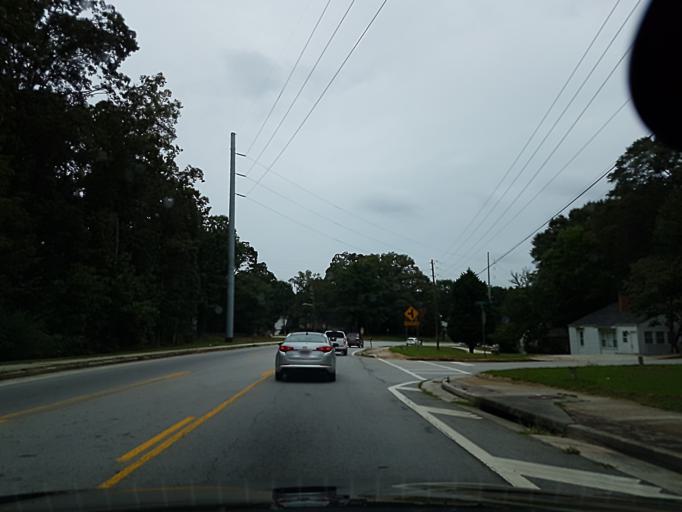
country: US
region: Georgia
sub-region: DeKalb County
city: Clarkston
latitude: 33.8293
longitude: -84.2589
